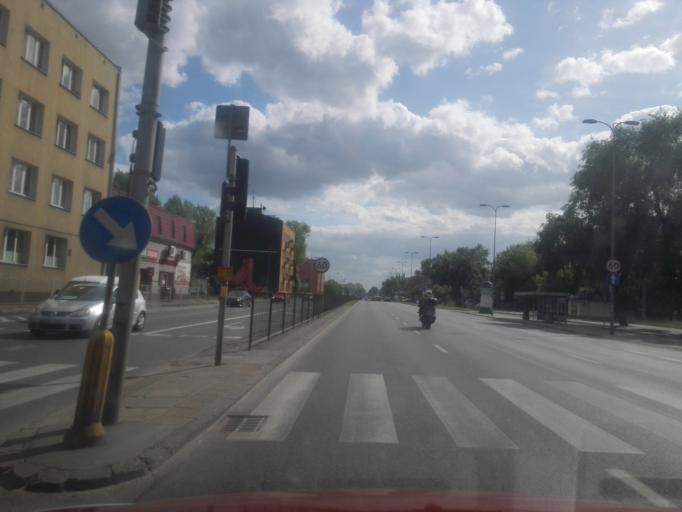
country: PL
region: Masovian Voivodeship
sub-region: Warszawa
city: Targowek
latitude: 52.2728
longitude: 21.0637
